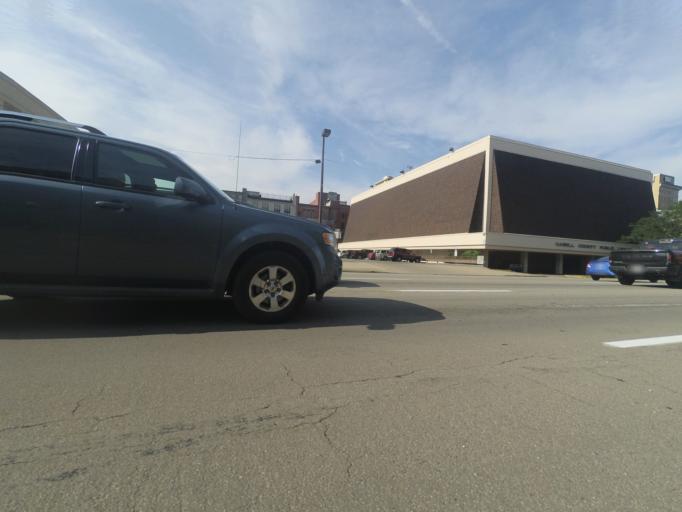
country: US
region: West Virginia
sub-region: Cabell County
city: Huntington
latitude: 38.4192
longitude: -82.4443
